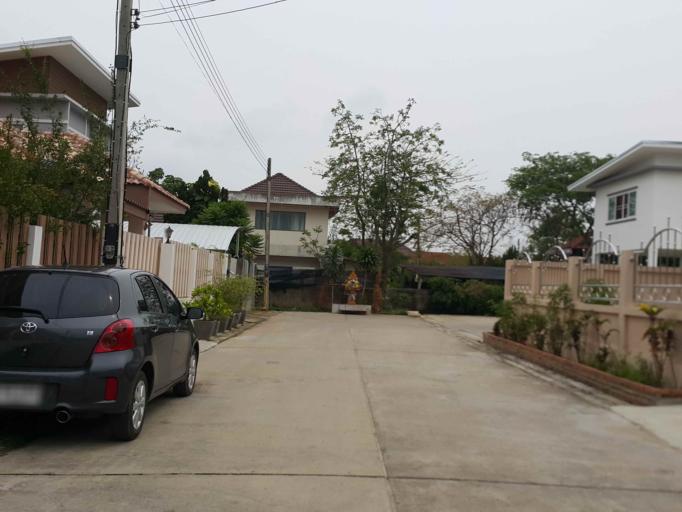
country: TH
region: Chiang Mai
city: Saraphi
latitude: 18.7507
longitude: 99.0130
